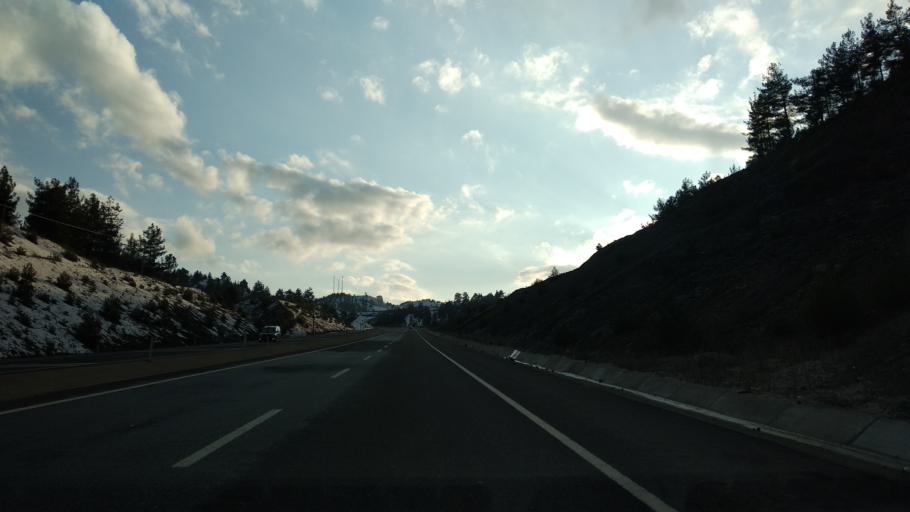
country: TR
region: Kahramanmaras
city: Yenicekale
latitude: 37.7340
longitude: 36.7019
